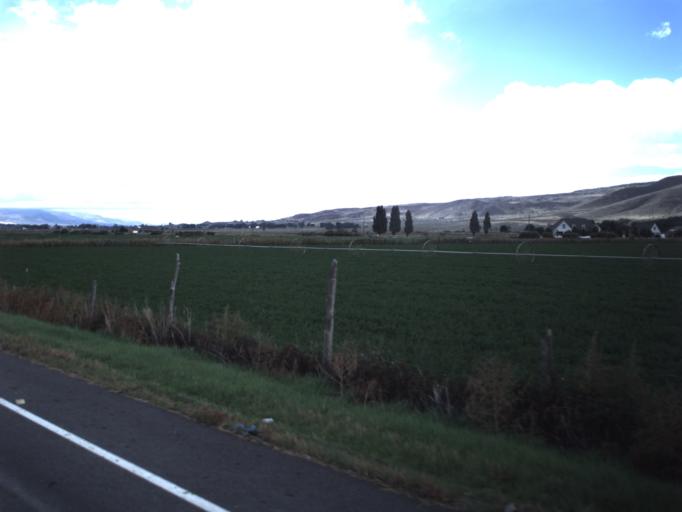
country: US
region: Utah
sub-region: Sevier County
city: Monroe
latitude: 38.6419
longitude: -112.1214
